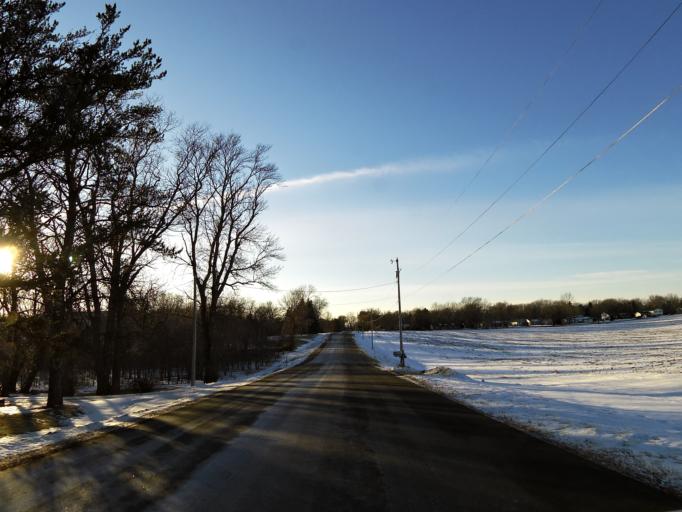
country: US
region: Minnesota
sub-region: Washington County
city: Cottage Grove
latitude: 44.8371
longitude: -92.8741
